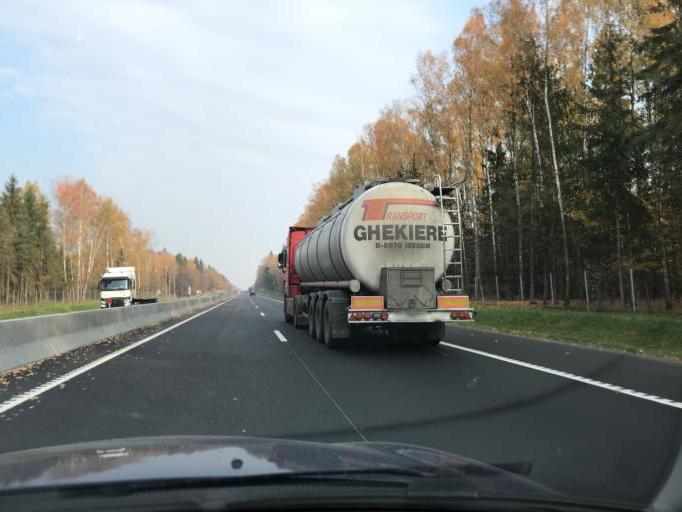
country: BY
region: Grodnenskaya
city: Shchuchin
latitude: 53.6859
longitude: 24.8604
